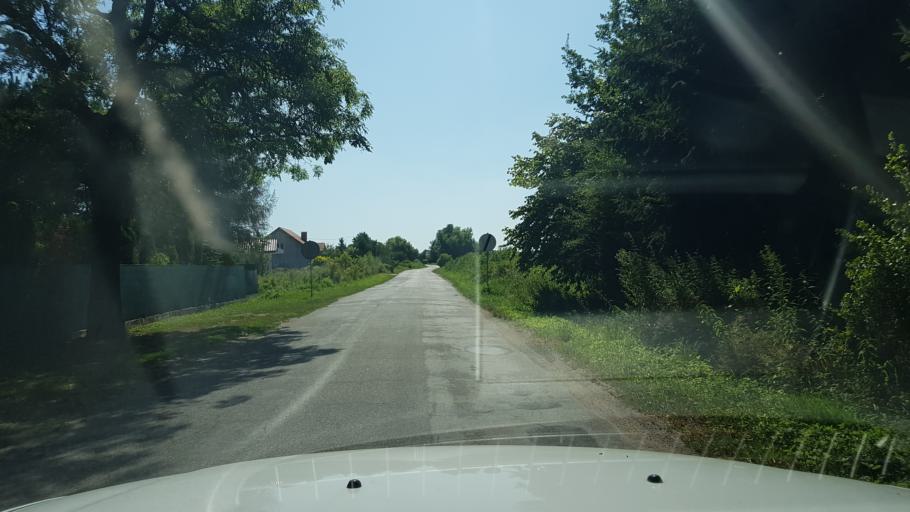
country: PL
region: West Pomeranian Voivodeship
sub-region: Powiat goleniowski
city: Goleniow
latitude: 53.4609
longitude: 14.7140
